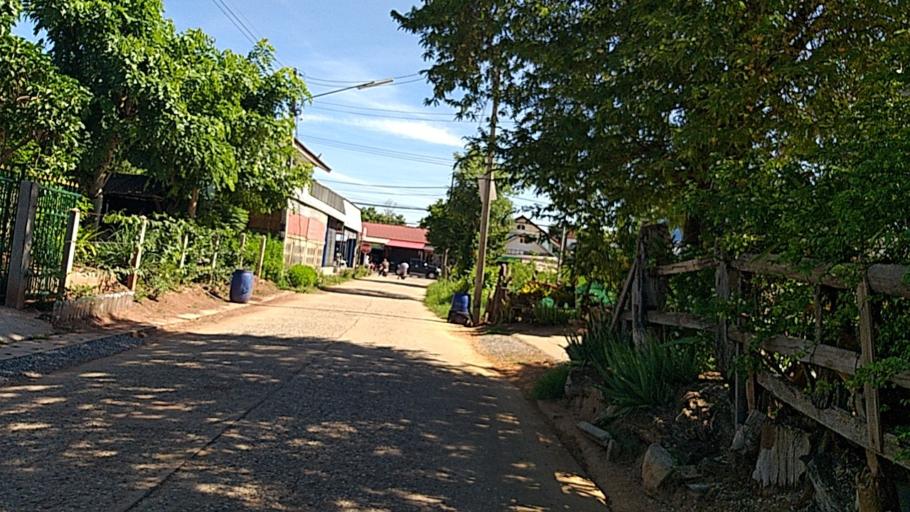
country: TH
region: Chaiyaphum
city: Ban Thaen
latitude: 16.4088
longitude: 102.3551
